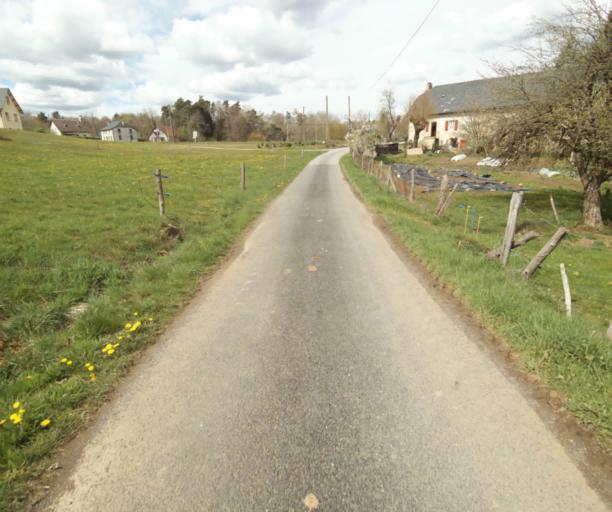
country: FR
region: Limousin
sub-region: Departement de la Correze
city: Argentat
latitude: 45.2025
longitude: 1.8935
